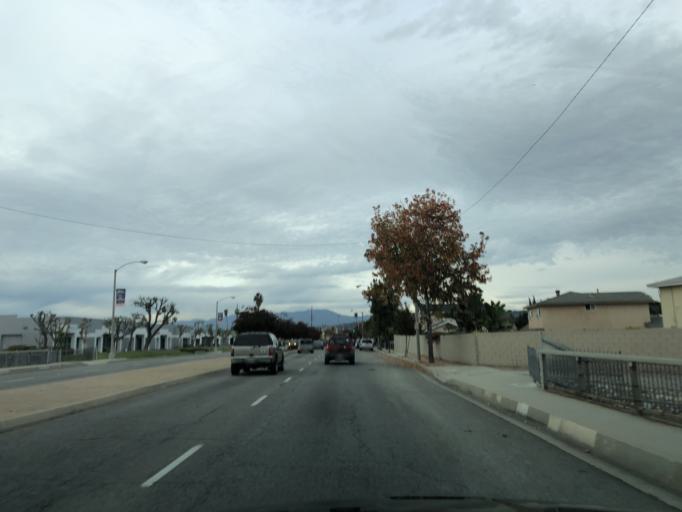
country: US
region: California
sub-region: Los Angeles County
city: South Whittier
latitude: 33.9463
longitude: -118.0464
